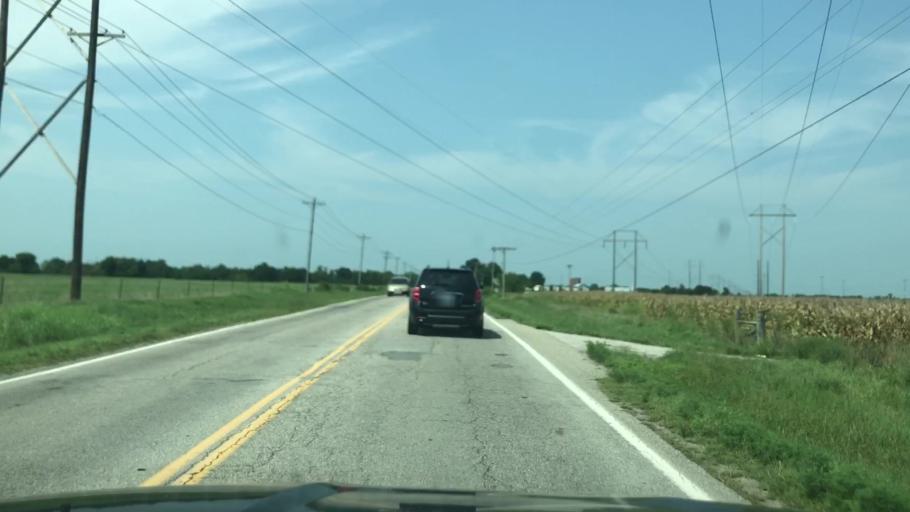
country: US
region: Oklahoma
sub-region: Ottawa County
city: Miami
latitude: 36.8881
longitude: -94.8418
